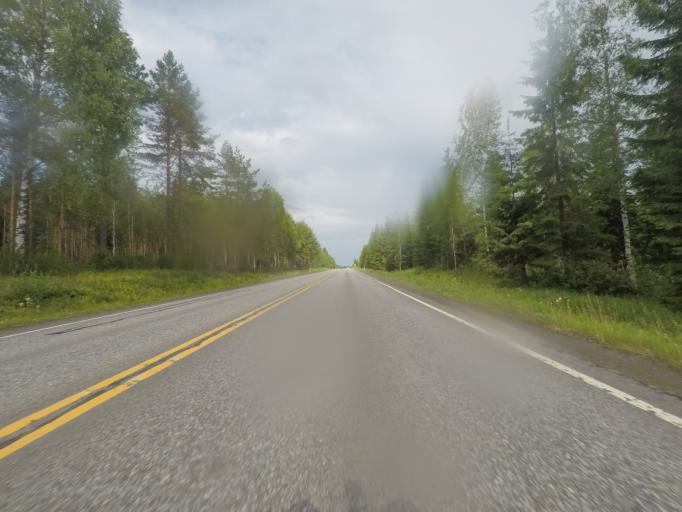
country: FI
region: Southern Savonia
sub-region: Savonlinna
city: Rantasalmi
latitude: 61.9596
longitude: 28.2220
